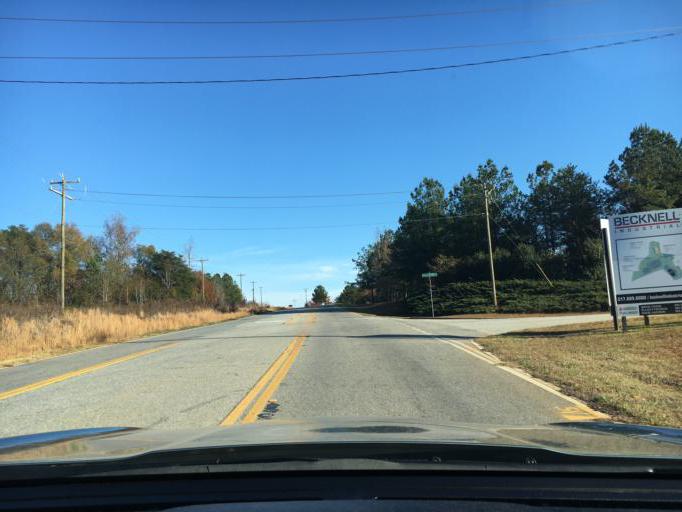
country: US
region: South Carolina
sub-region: Spartanburg County
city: Southern Shops
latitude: 34.9947
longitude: -82.0439
